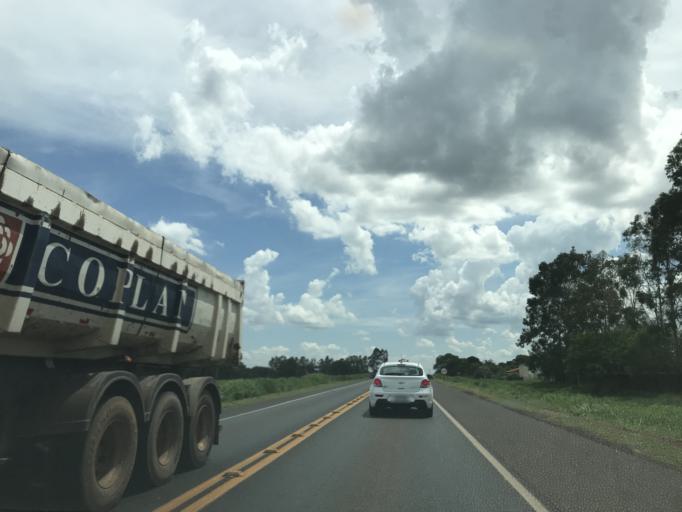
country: BR
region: Sao Paulo
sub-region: Nova Granada
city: Nova Granada
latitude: -20.2817
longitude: -49.1948
